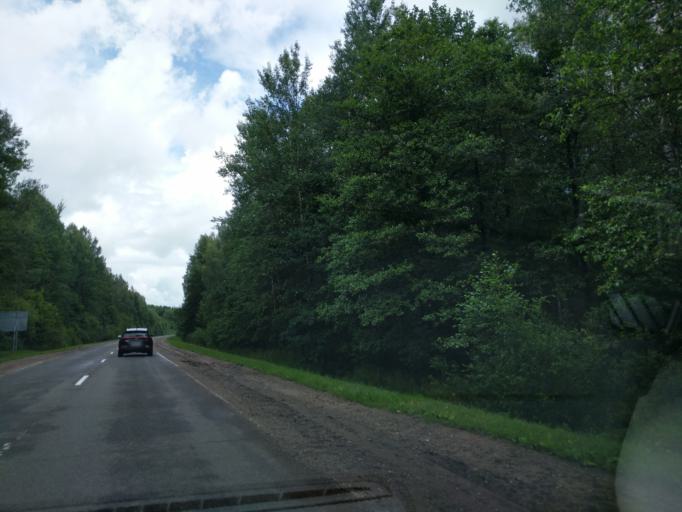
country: BY
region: Minsk
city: Il'ya
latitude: 54.4154
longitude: 27.2639
